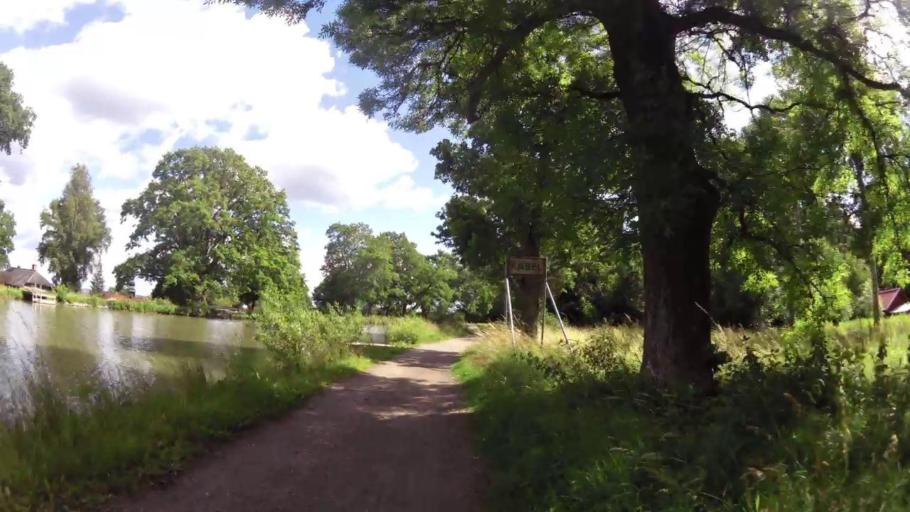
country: SE
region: OEstergoetland
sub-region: Linkopings Kommun
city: Berg
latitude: 58.4986
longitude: 15.5146
